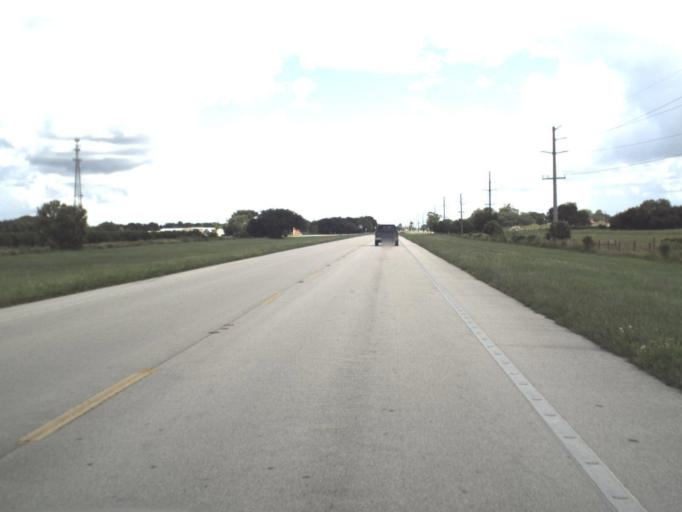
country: US
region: Florida
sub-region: DeSoto County
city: Southeast Arcadia
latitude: 27.2095
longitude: -81.6823
